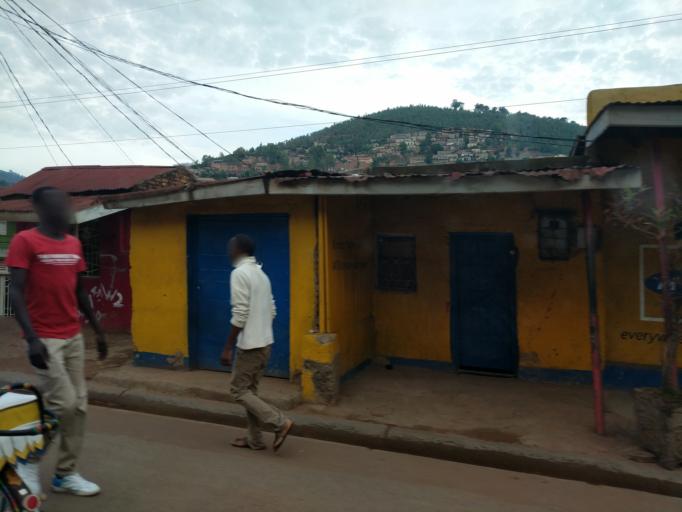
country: RW
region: Kigali
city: Kigali
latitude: -1.9430
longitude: 30.0399
